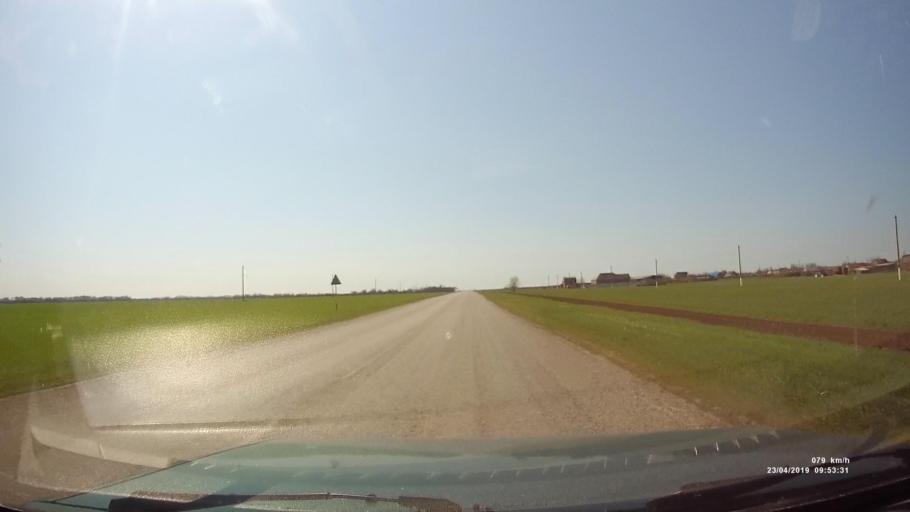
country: RU
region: Rostov
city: Orlovskiy
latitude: 46.8320
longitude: 42.0506
